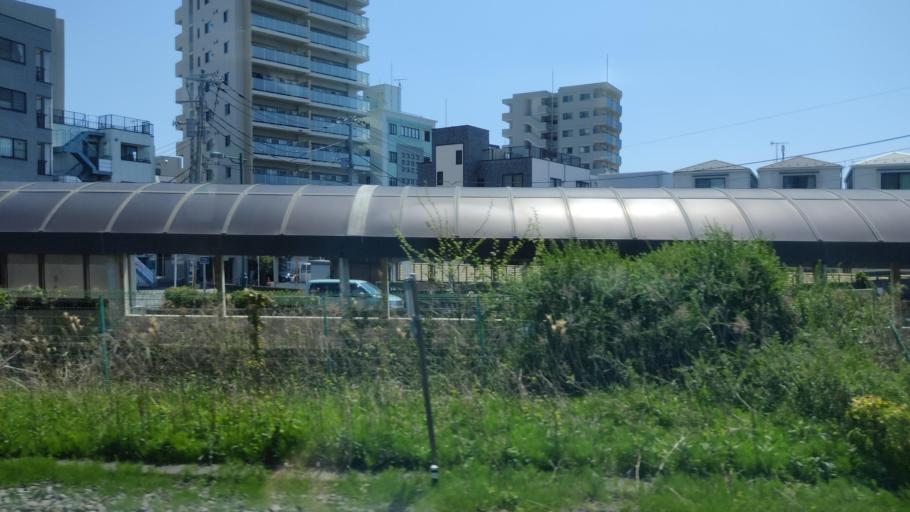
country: JP
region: Kanagawa
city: Chigasaki
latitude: 35.3294
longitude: 139.4043
